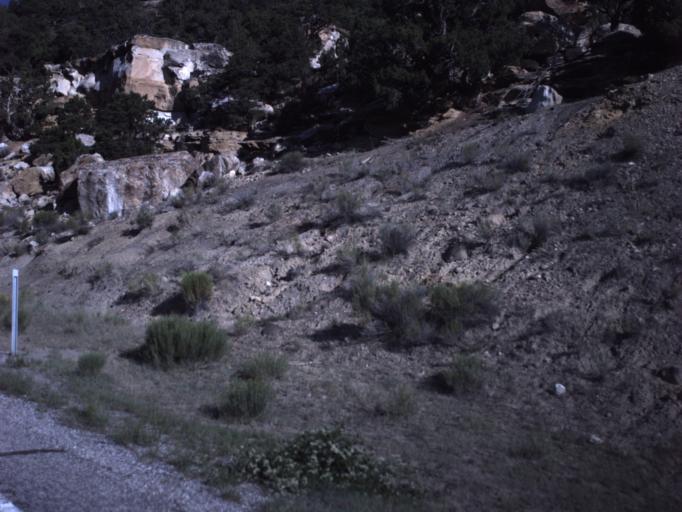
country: US
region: Utah
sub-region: Wayne County
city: Loa
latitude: 38.6723
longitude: -111.4128
